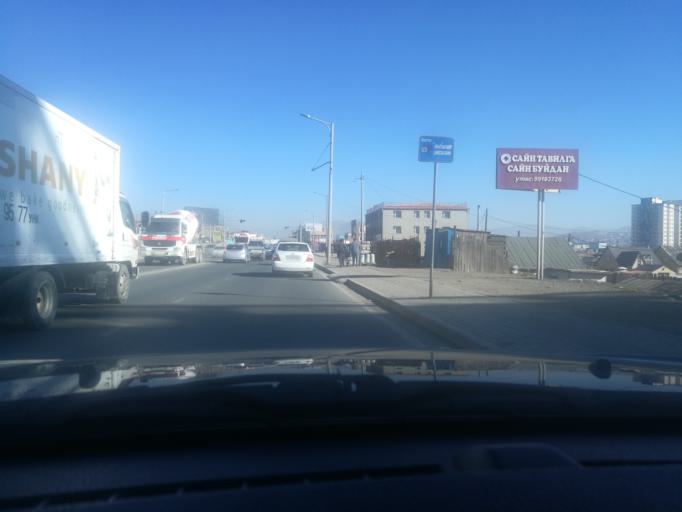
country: MN
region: Ulaanbaatar
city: Ulaanbaatar
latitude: 47.9355
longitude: 106.9079
